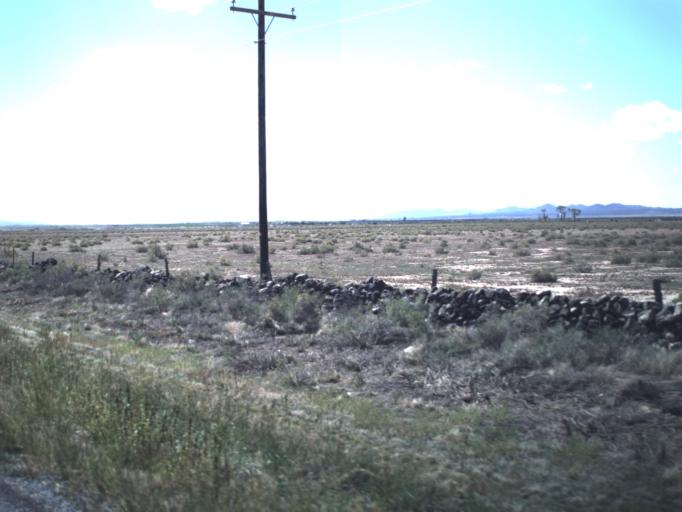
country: US
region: Utah
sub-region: Iron County
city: Enoch
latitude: 37.8666
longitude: -113.0317
